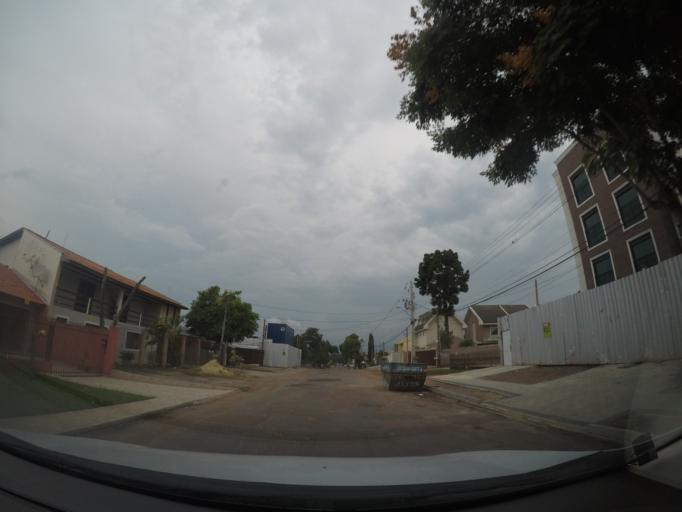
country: BR
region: Parana
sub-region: Sao Jose Dos Pinhais
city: Sao Jose dos Pinhais
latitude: -25.5148
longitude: -49.2365
